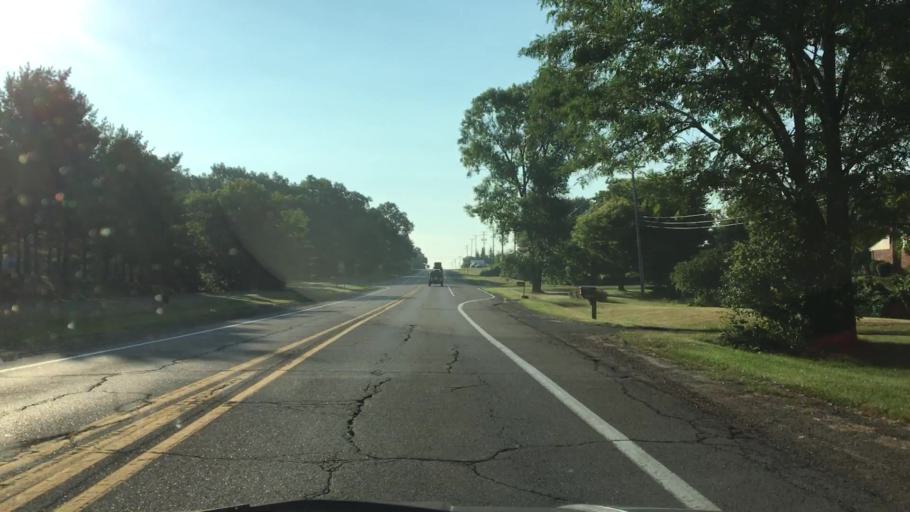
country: US
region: Michigan
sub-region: Oakland County
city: South Lyon
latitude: 42.5163
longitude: -83.6377
